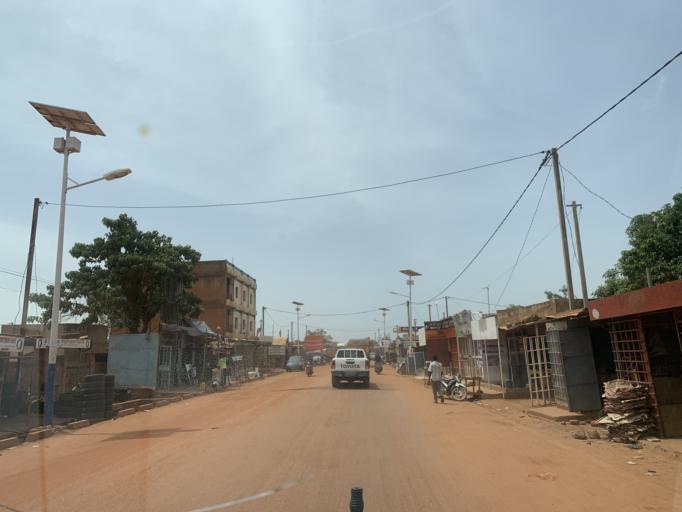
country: BF
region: Centre
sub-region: Kadiogo Province
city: Ouagadougou
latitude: 12.3288
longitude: -1.4877
